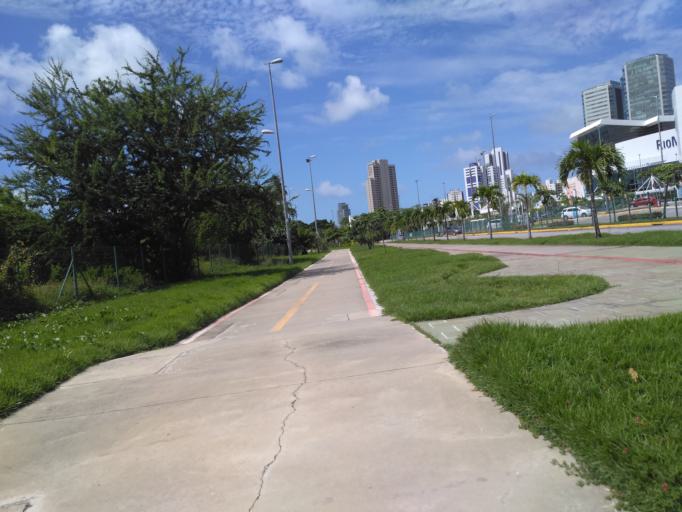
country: BR
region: Pernambuco
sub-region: Recife
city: Recife
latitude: -8.0842
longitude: -34.8965
